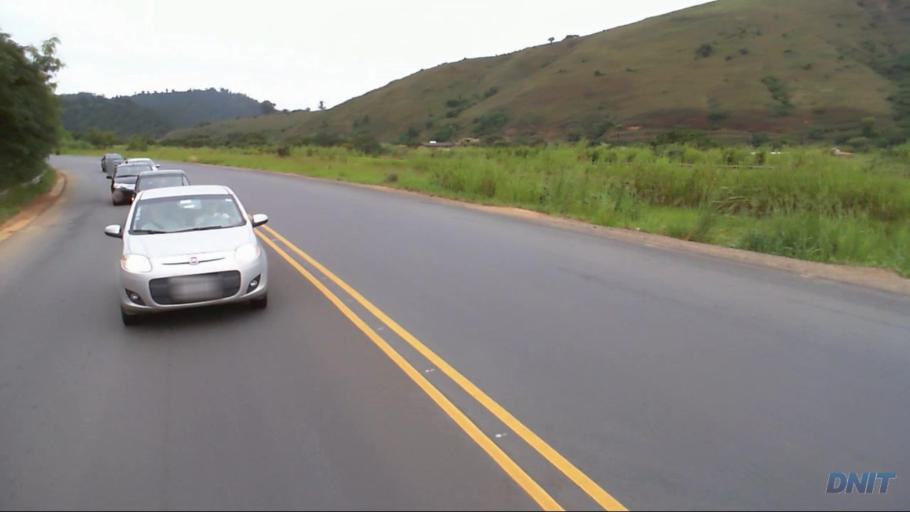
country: BR
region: Minas Gerais
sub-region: Coronel Fabriciano
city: Coronel Fabriciano
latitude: -19.5342
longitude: -42.5975
